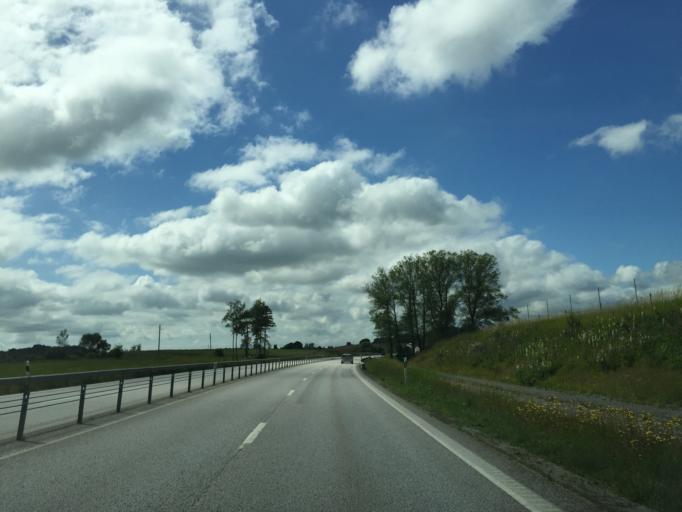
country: SE
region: Skane
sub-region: Skurups Kommun
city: Skurup
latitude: 55.4977
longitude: 13.4198
